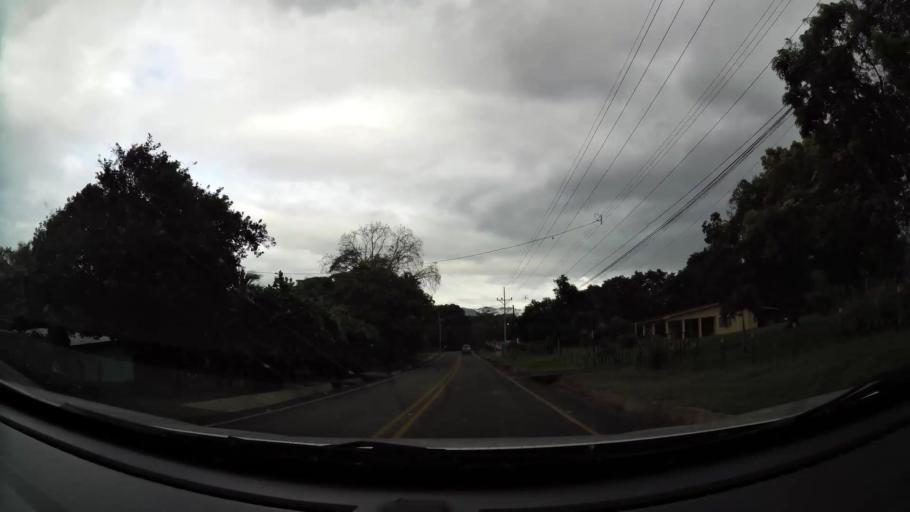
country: CR
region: Alajuela
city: Orotina
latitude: 9.9555
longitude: -84.5781
